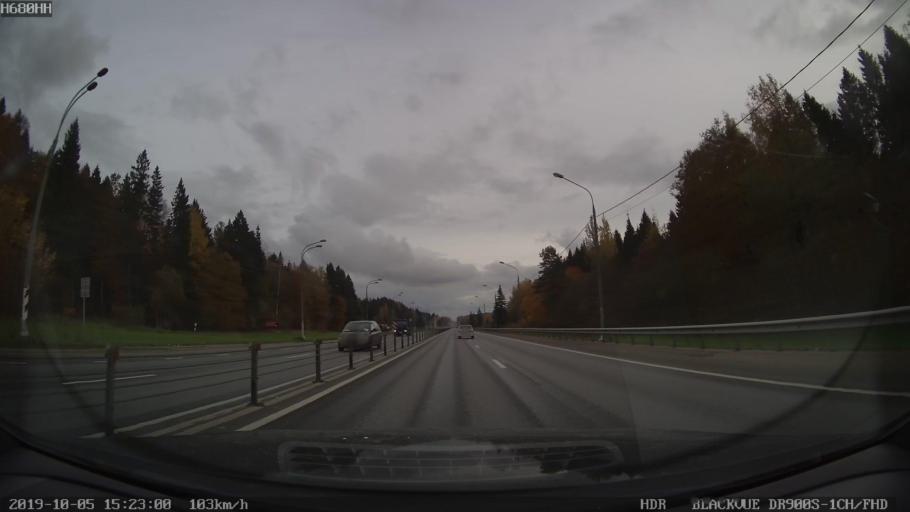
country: RU
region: Moskovskaya
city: Solnechnogorsk
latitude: 56.2140
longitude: 36.9351
